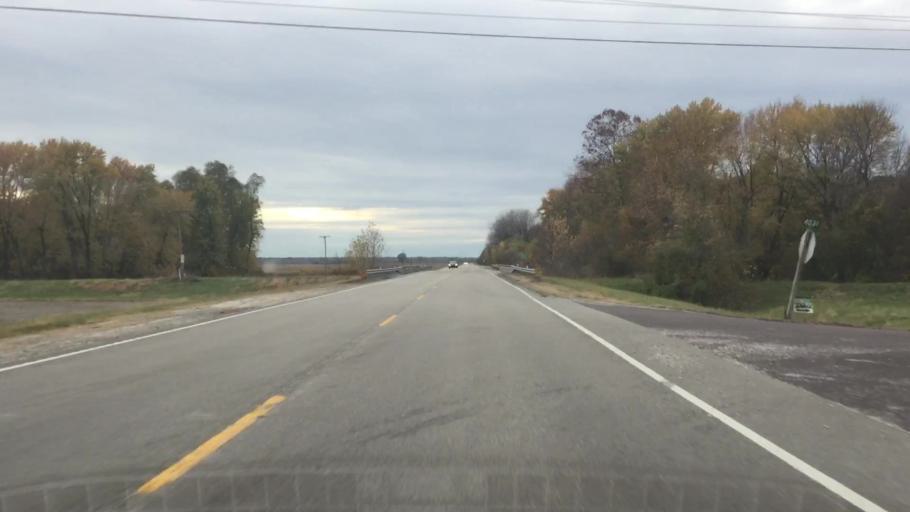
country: US
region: Missouri
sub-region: Callaway County
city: Holts Summit
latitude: 38.5825
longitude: -92.0623
